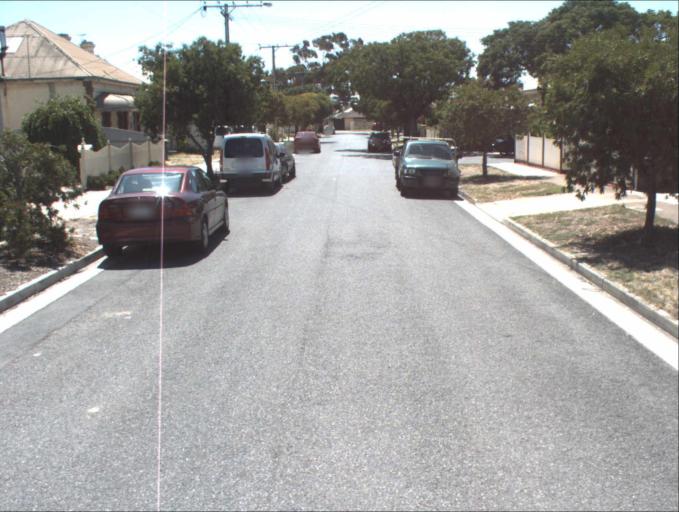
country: AU
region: South Australia
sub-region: Port Adelaide Enfield
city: Birkenhead
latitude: -34.8370
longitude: 138.4988
